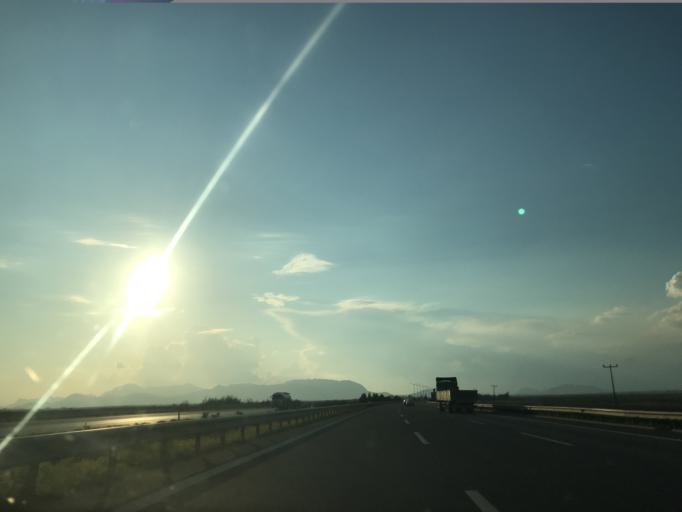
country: TR
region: Adana
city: Ceyhan
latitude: 36.9815
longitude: 35.8742
